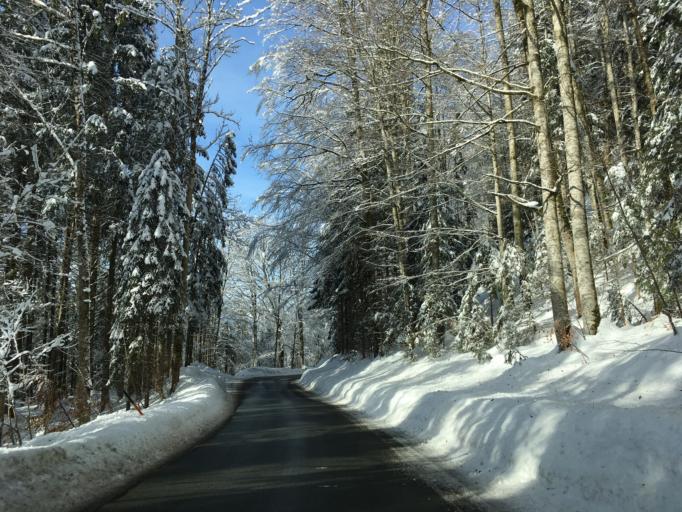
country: DE
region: Bavaria
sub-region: Upper Bavaria
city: Burg Unter-Falkenstein
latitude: 47.6656
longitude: 12.1101
